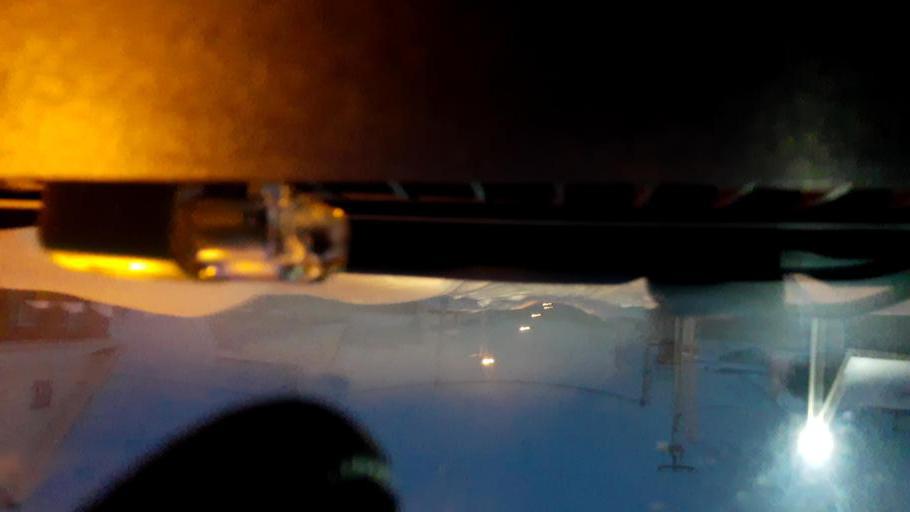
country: RU
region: Bashkortostan
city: Iglino
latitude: 54.7916
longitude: 56.2713
